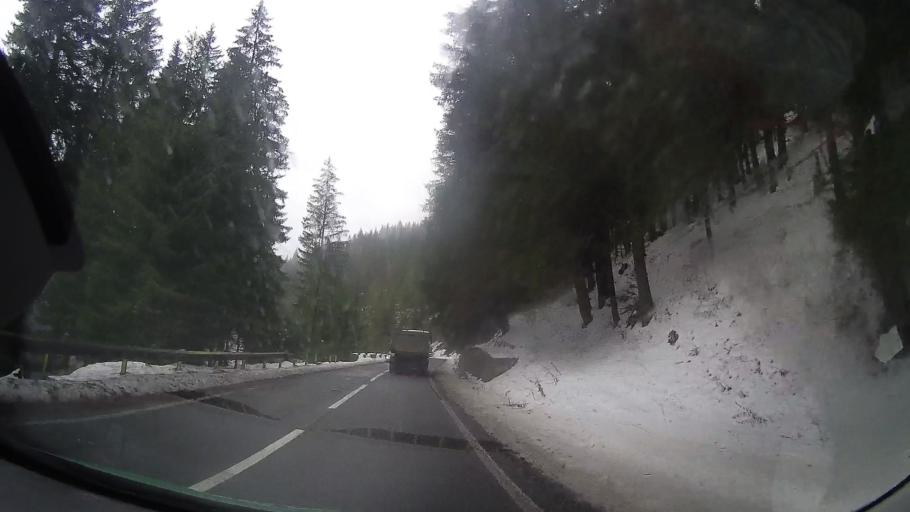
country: RO
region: Neamt
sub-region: Comuna Bicaz Chei
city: Bicaz Chei
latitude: 46.7793
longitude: 25.7593
